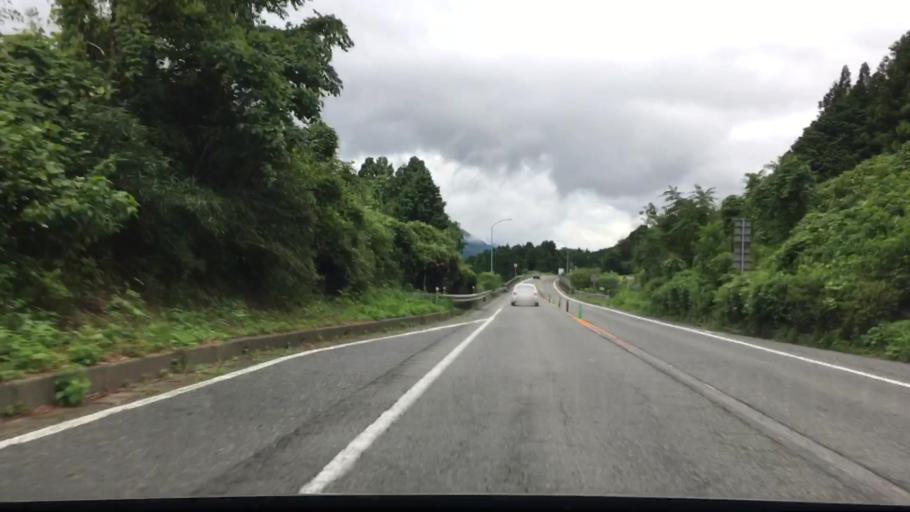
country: JP
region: Hyogo
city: Nishiwaki
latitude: 35.1009
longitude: 134.7773
